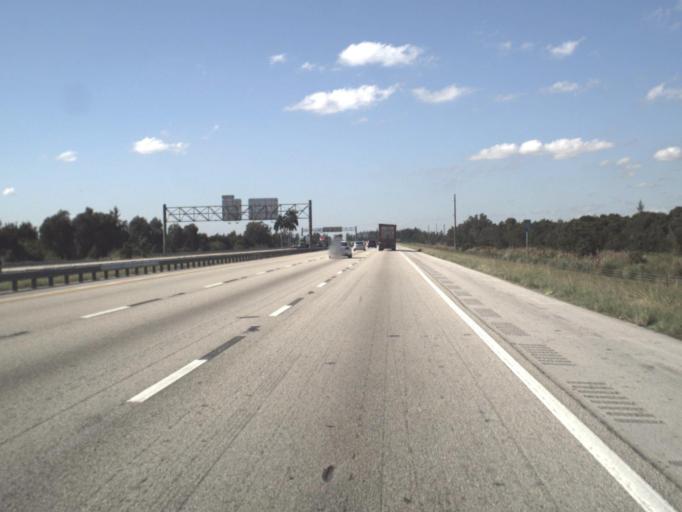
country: US
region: Florida
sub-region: Miami-Dade County
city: Palm Springs North
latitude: 25.9398
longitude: -80.3625
